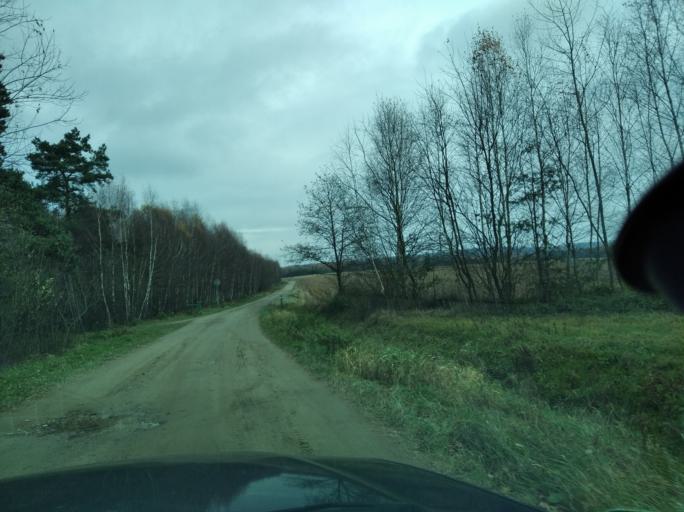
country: PL
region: Subcarpathian Voivodeship
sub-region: Powiat strzyzowski
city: Wysoka Strzyzowska
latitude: 49.7984
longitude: 21.7811
